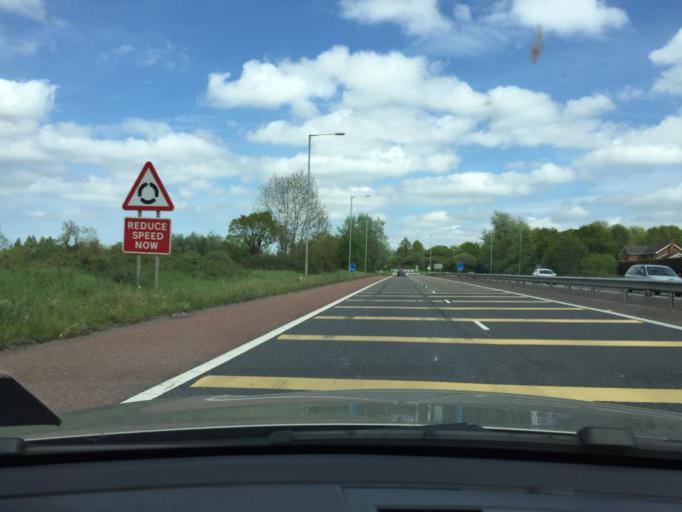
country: GB
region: Northern Ireland
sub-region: Craigavon District
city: Craigavon
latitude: 54.4610
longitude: -6.4196
